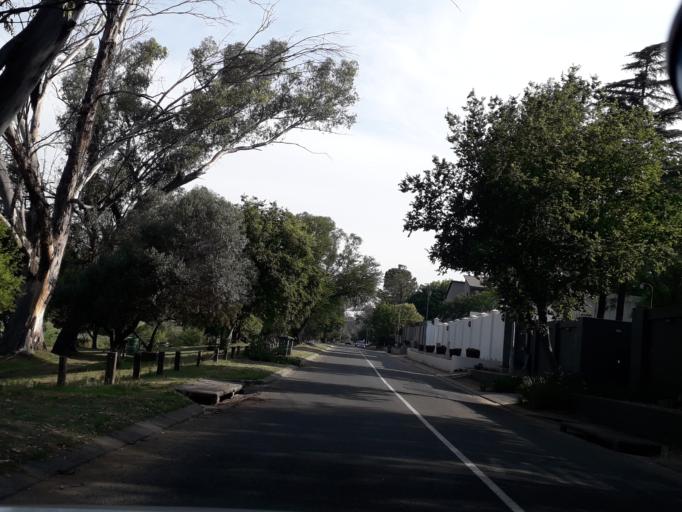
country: ZA
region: Gauteng
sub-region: City of Johannesburg Metropolitan Municipality
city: Midrand
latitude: -26.0632
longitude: 28.0418
